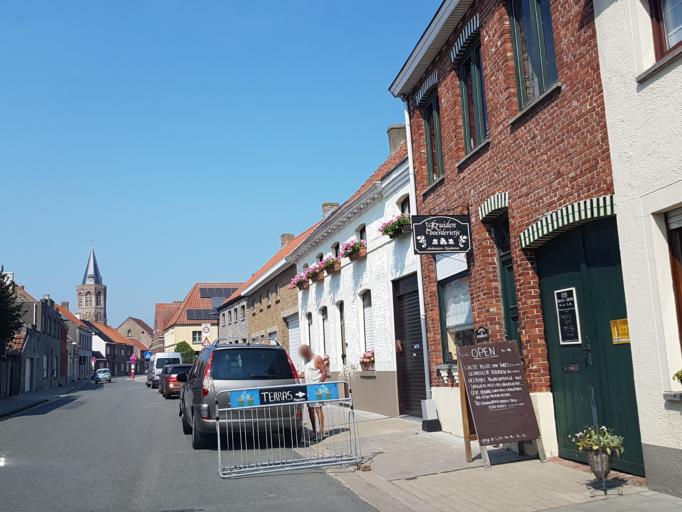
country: BE
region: Flanders
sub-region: Provincie West-Vlaanderen
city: Jabbeke
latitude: 51.2126
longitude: 3.0735
